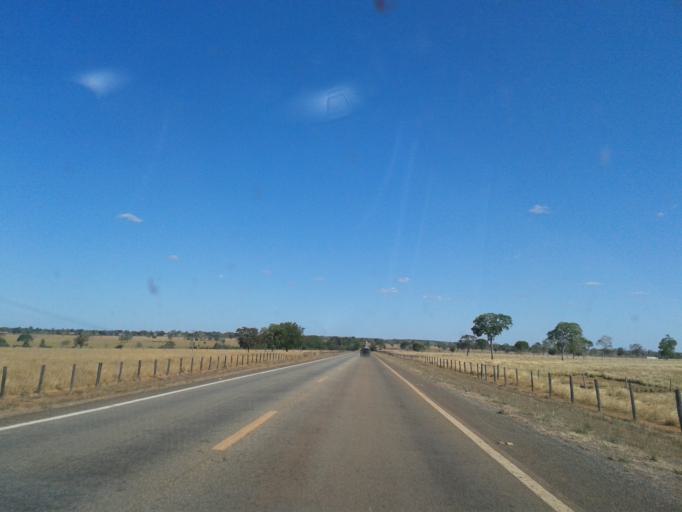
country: BR
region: Goias
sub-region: Mozarlandia
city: Mozarlandia
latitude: -14.2653
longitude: -50.3988
